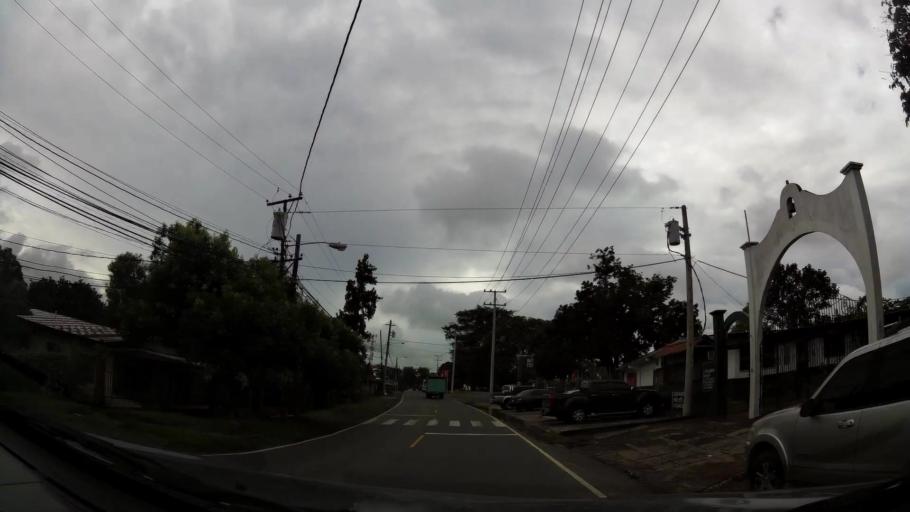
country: PA
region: Chiriqui
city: David
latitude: 8.4368
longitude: -82.4217
